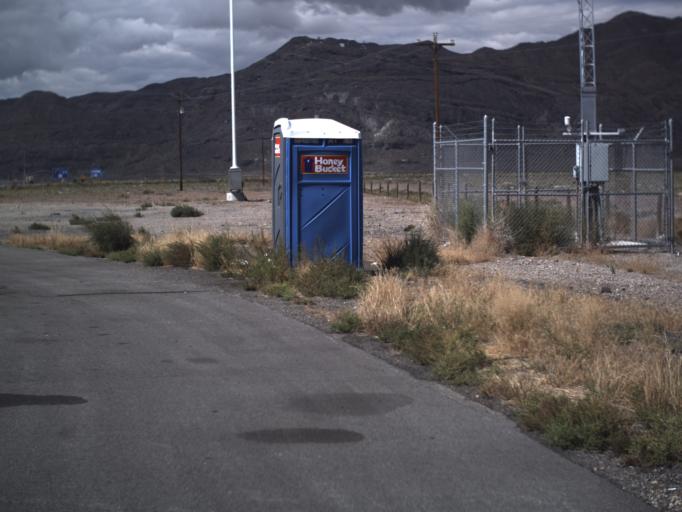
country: US
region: Utah
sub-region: Tooele County
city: Wendover
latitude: 40.7459
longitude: -113.9906
